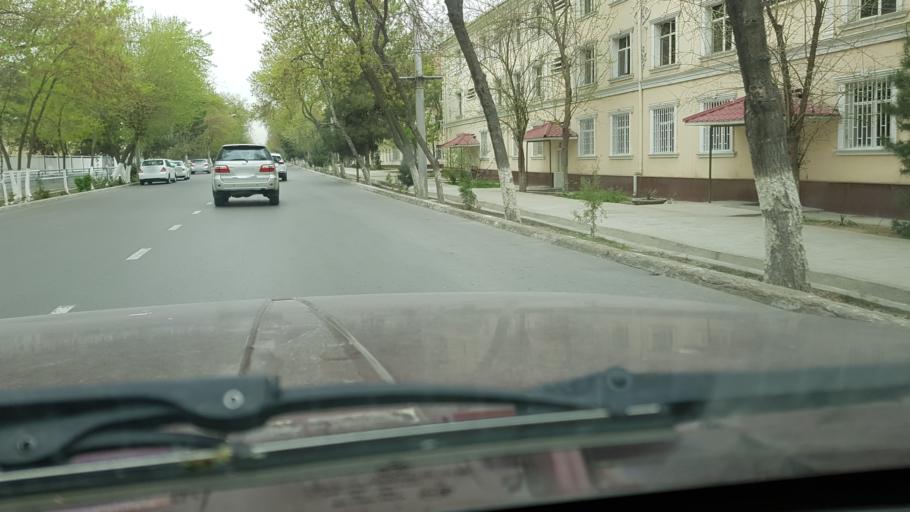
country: TM
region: Ahal
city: Ashgabat
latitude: 37.9458
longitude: 58.3597
